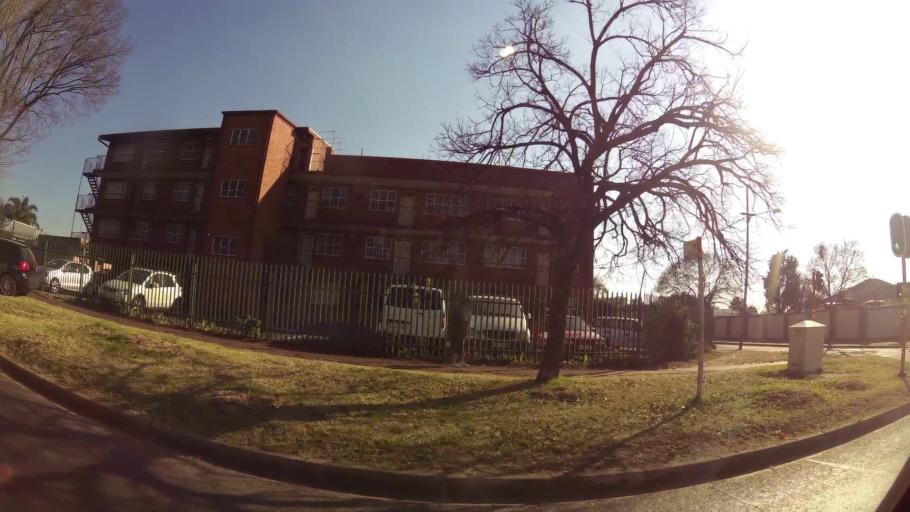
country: ZA
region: Gauteng
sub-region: Ekurhuleni Metropolitan Municipality
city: Germiston
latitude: -26.1987
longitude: 28.1267
